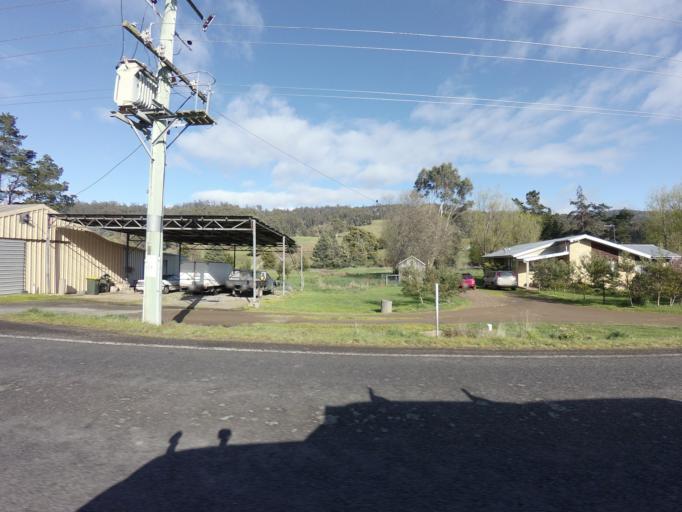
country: AU
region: Tasmania
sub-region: Huon Valley
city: Cygnet
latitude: -43.2937
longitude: 147.0114
